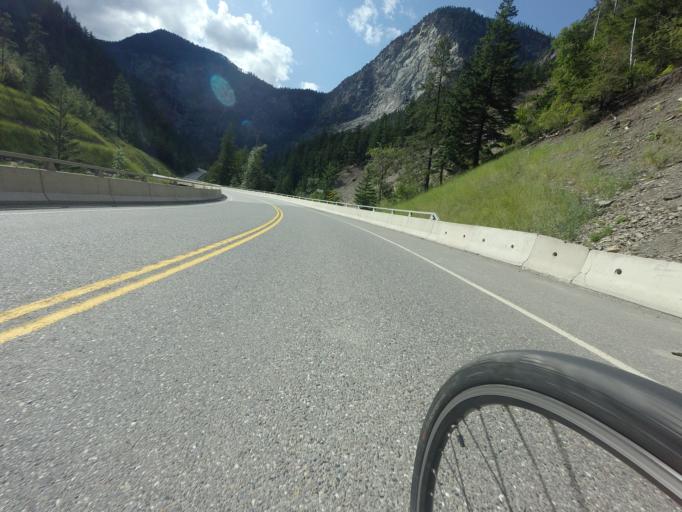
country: CA
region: British Columbia
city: Lillooet
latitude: 50.6440
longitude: -122.0531
